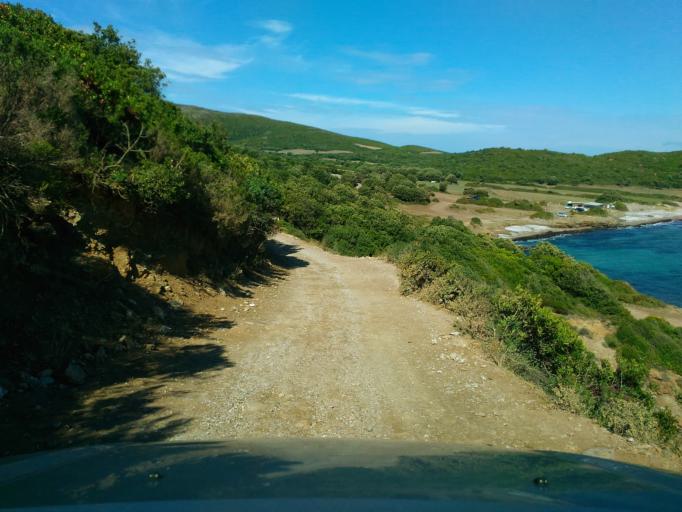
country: FR
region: Corsica
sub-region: Departement de la Haute-Corse
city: Brando
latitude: 42.9719
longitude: 9.4546
